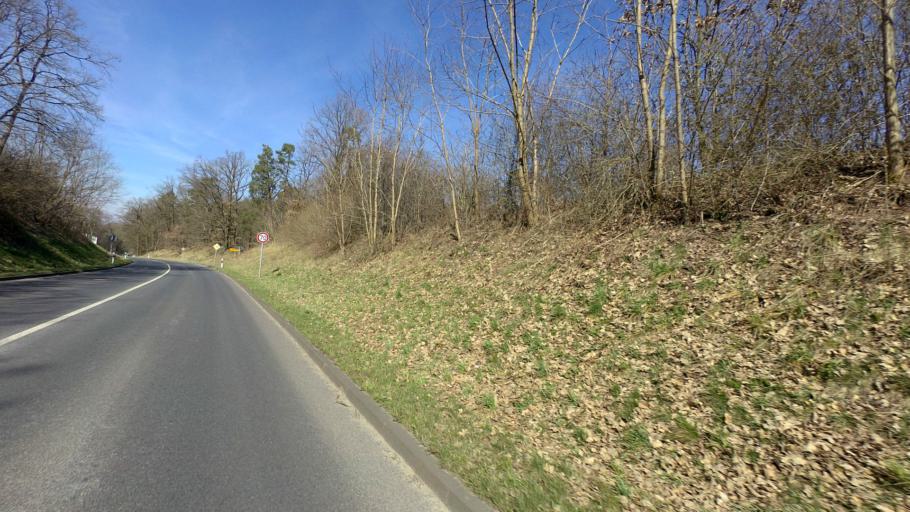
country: DE
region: Brandenburg
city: Furstenwalde
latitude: 52.3982
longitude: 14.0466
